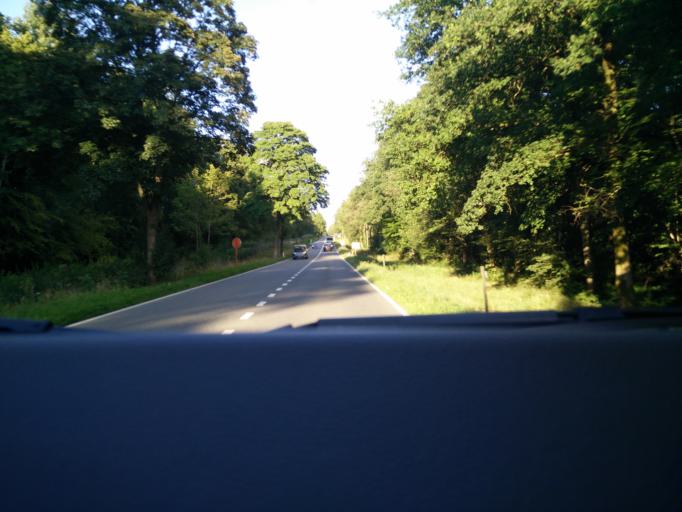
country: BE
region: Wallonia
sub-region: Province de Namur
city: Florennes
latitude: 50.2226
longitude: 4.6460
